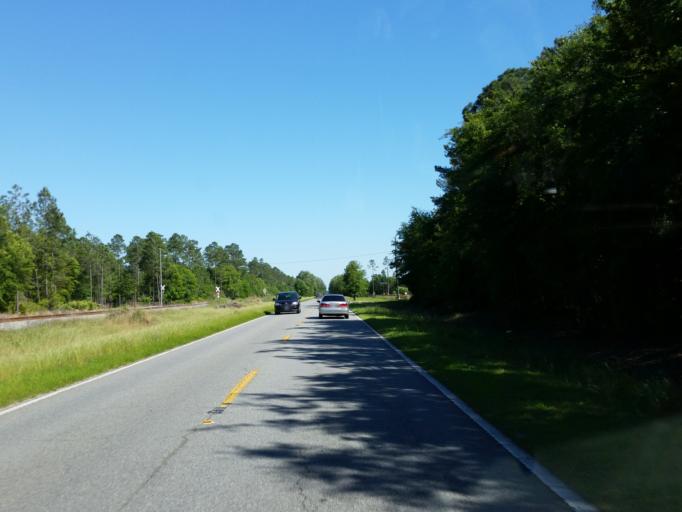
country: US
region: Georgia
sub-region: Echols County
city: Statenville
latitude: 30.6591
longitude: -83.1538
